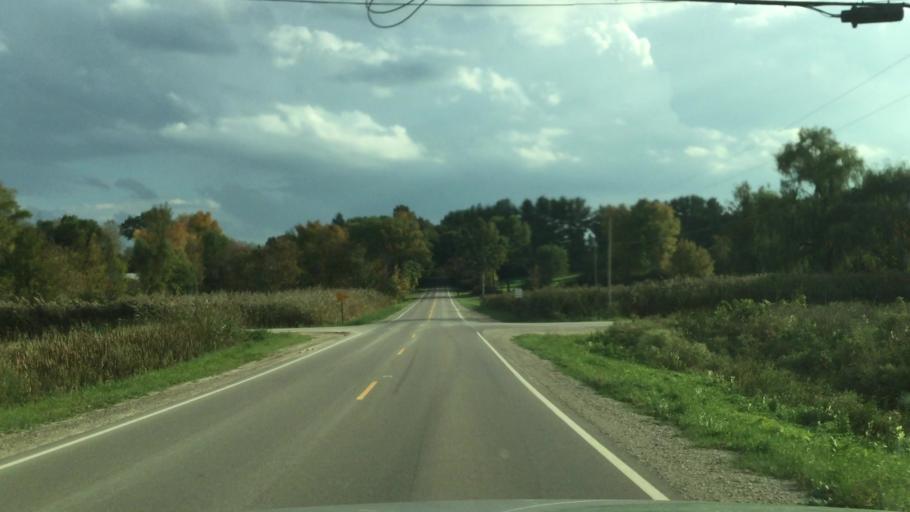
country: US
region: Michigan
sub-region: Genesee County
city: Fenton
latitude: 42.6791
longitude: -83.7022
